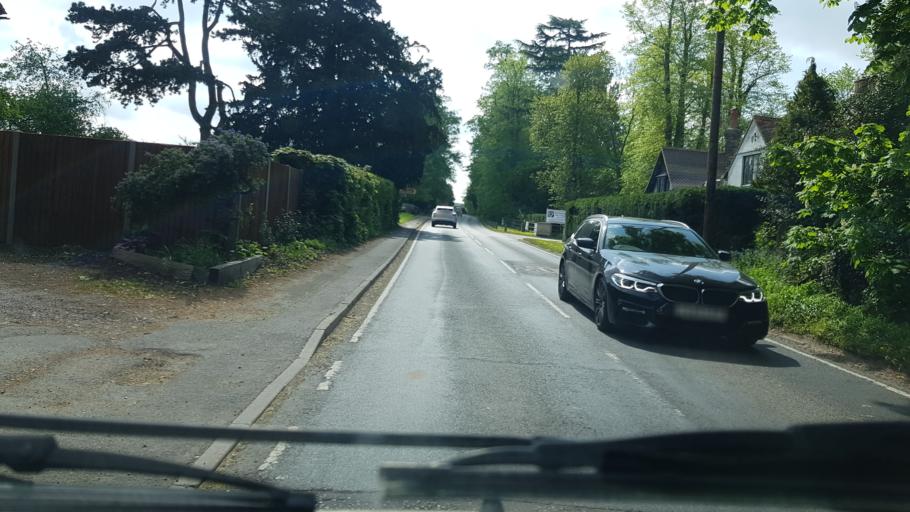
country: GB
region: England
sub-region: Surrey
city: Cobham
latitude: 51.3163
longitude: -0.3805
